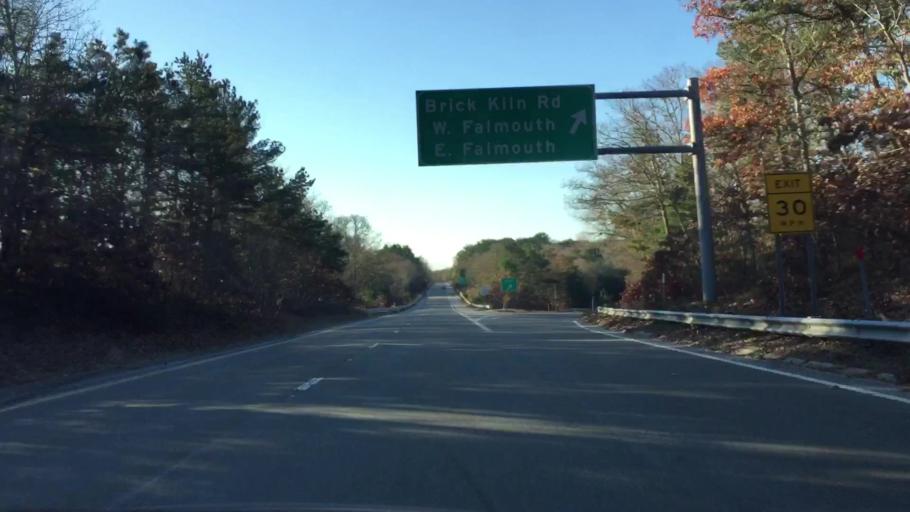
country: US
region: Massachusetts
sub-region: Barnstable County
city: West Falmouth
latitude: 41.5970
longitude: -70.6280
